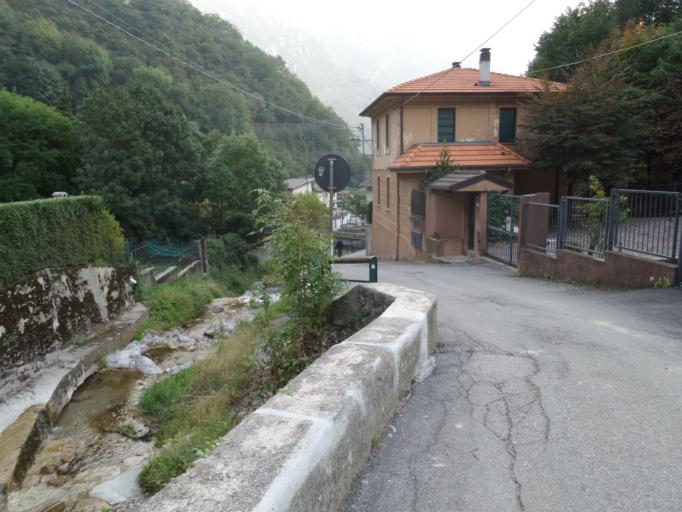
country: IT
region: Lombardy
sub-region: Provincia di Lecco
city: Ballabio
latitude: 45.9037
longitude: 9.4187
